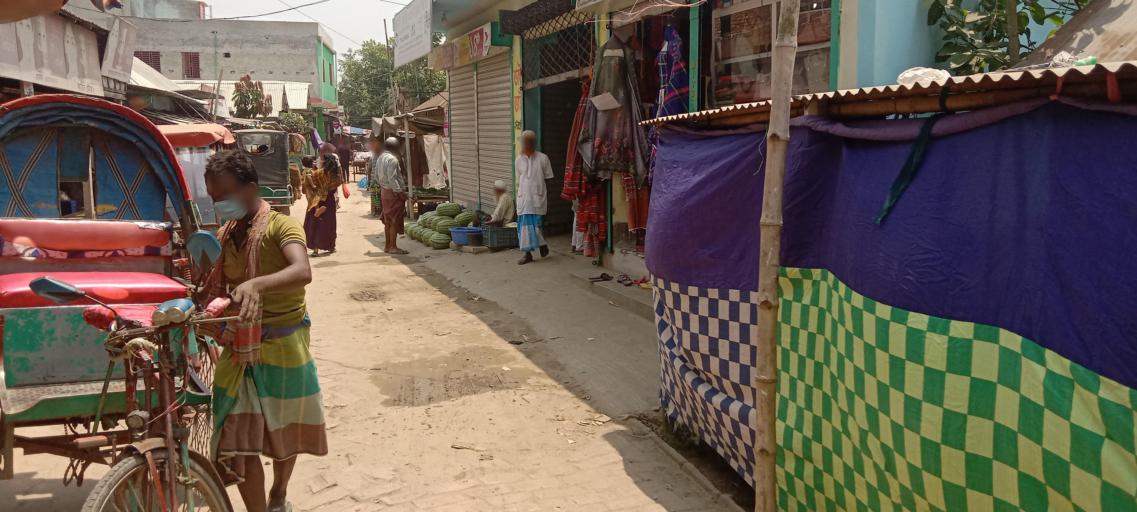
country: BD
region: Dhaka
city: Azimpur
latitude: 23.7052
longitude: 90.2849
